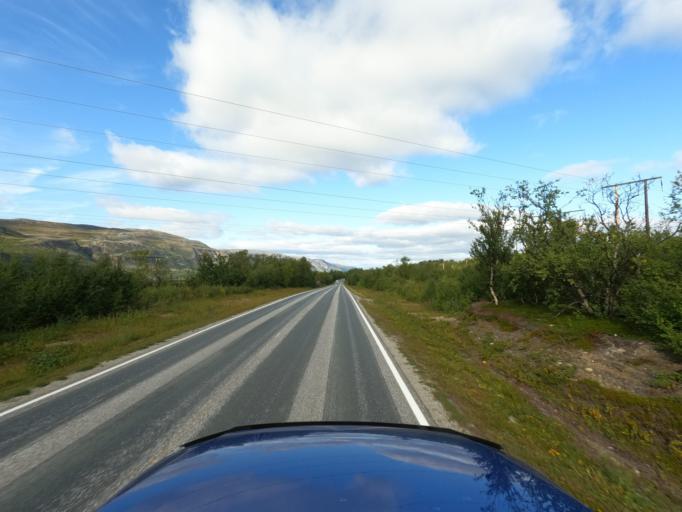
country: NO
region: Finnmark Fylke
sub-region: Porsanger
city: Lakselv
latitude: 69.9938
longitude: 24.9503
